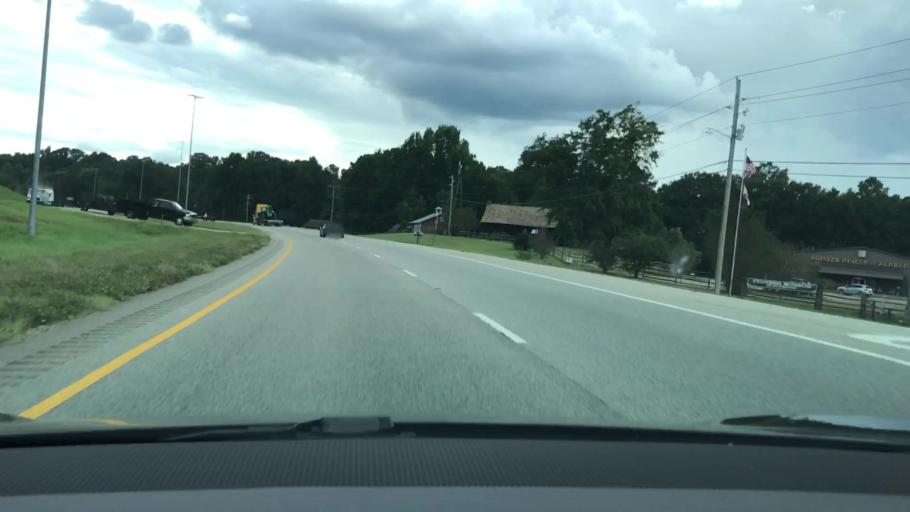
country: US
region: Alabama
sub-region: Pike County
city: Troy
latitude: 31.8256
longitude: -85.9949
